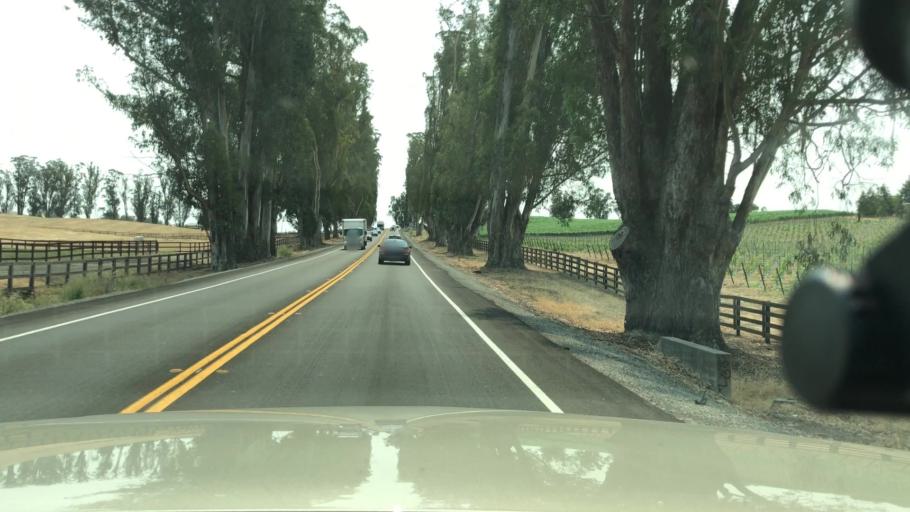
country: US
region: California
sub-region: Marin County
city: Black Point-Green Point
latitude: 38.1768
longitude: -122.5275
